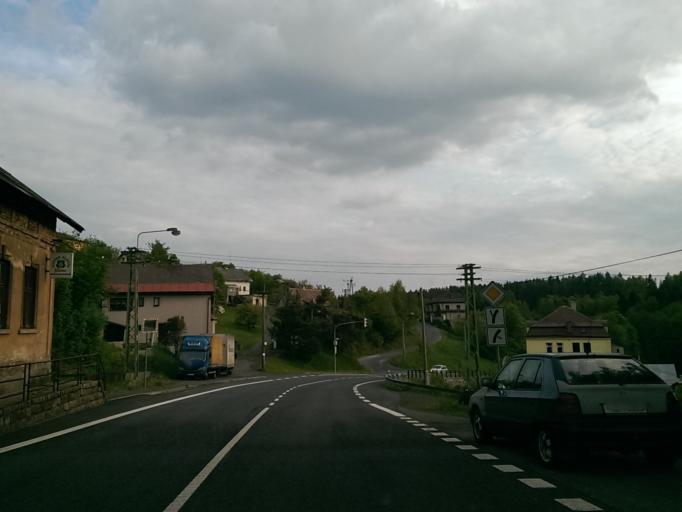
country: CZ
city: Pencin
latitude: 50.6803
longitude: 15.2677
